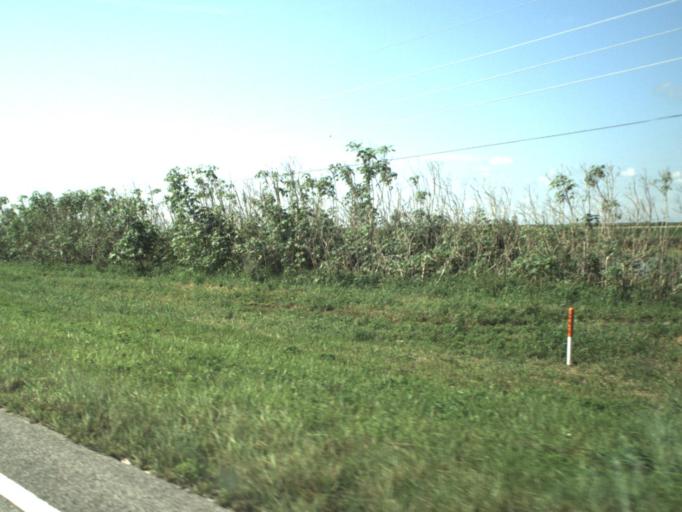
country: US
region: Florida
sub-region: Palm Beach County
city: Belle Glade Camp
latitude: 26.4178
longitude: -80.6021
